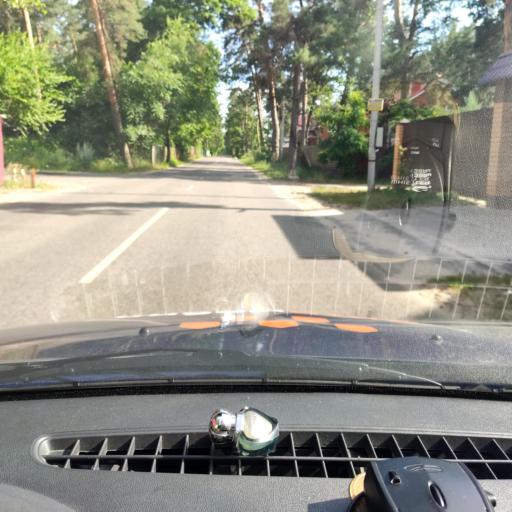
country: RU
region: Voronezj
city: Somovo
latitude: 51.7547
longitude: 39.3660
